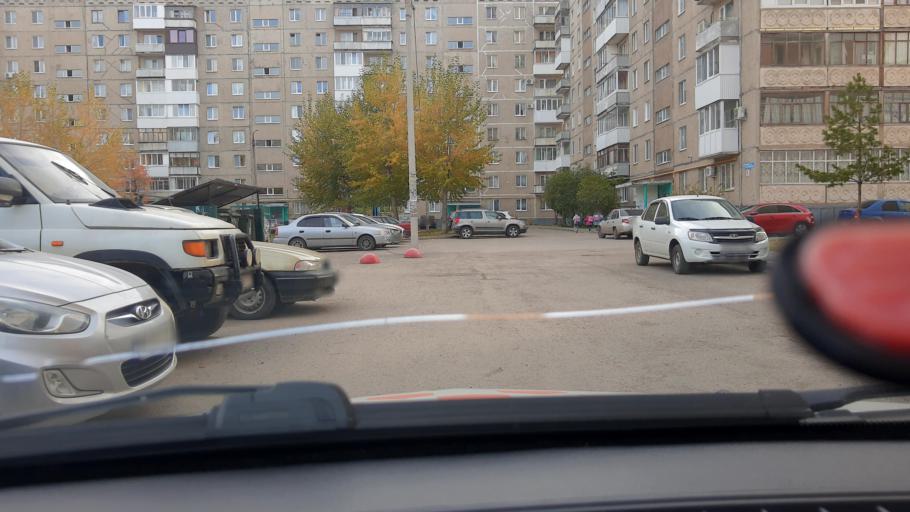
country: RU
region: Bashkortostan
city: Ufa
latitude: 54.7772
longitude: 56.1198
